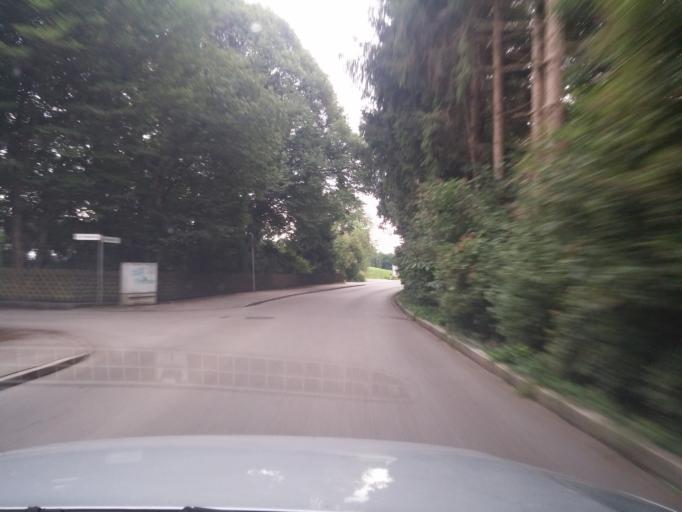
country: DE
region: Bavaria
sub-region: Swabia
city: Buxheim
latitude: 47.9934
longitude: 10.1370
